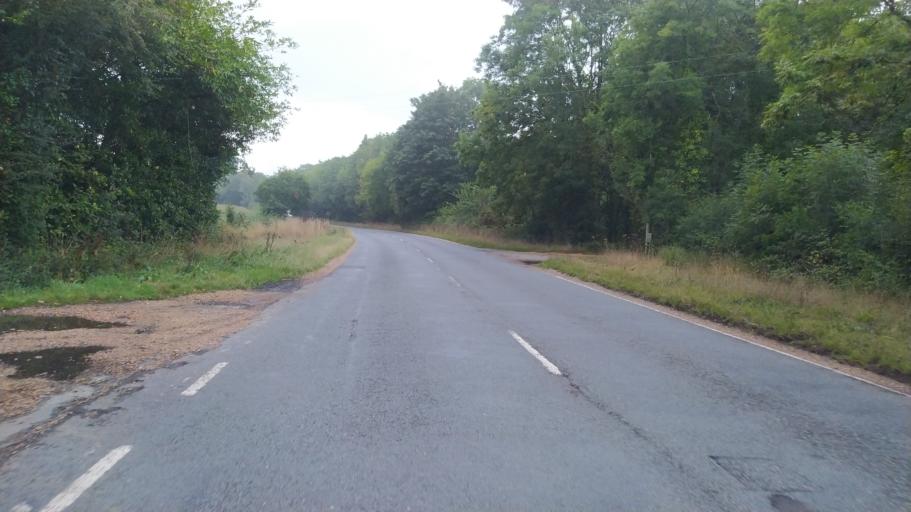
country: GB
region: England
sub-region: Hampshire
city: New Milton
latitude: 50.7759
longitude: -1.6960
